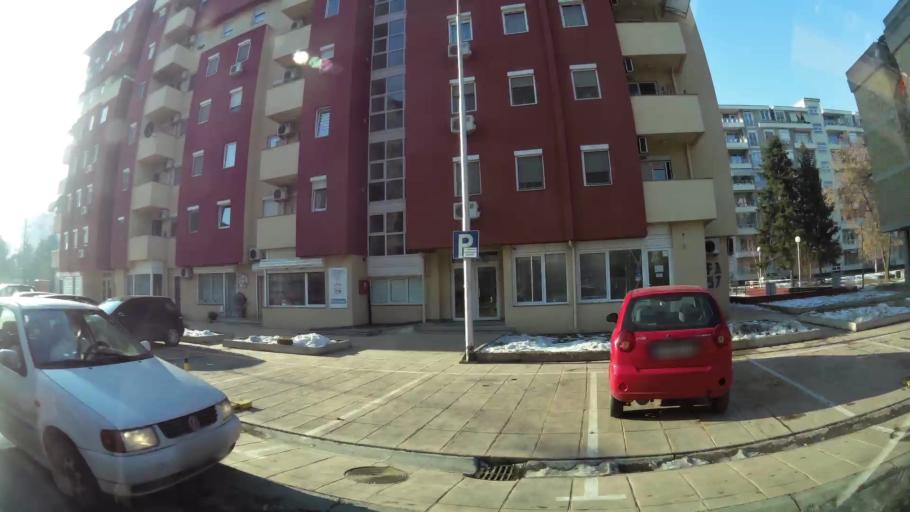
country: MK
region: Kisela Voda
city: Usje
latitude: 41.9828
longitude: 21.4574
